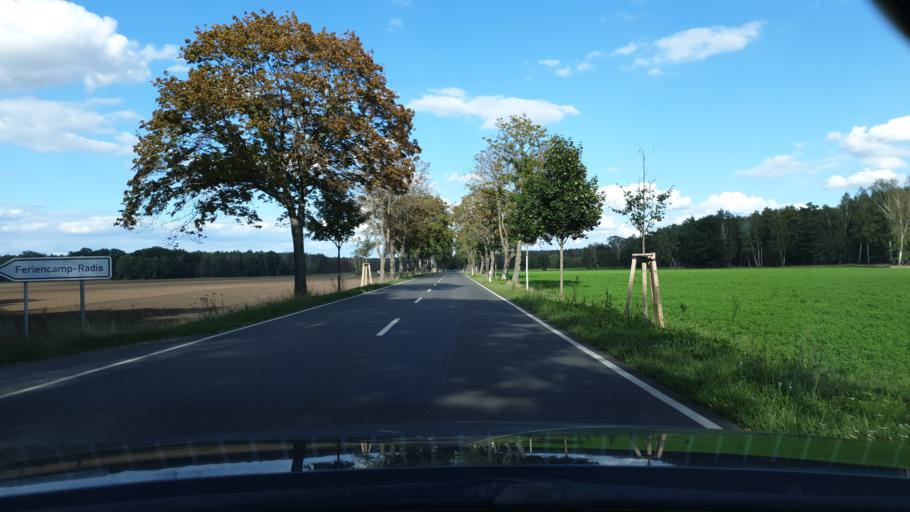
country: DE
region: Saxony-Anhalt
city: Radis
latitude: 51.7621
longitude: 12.5333
